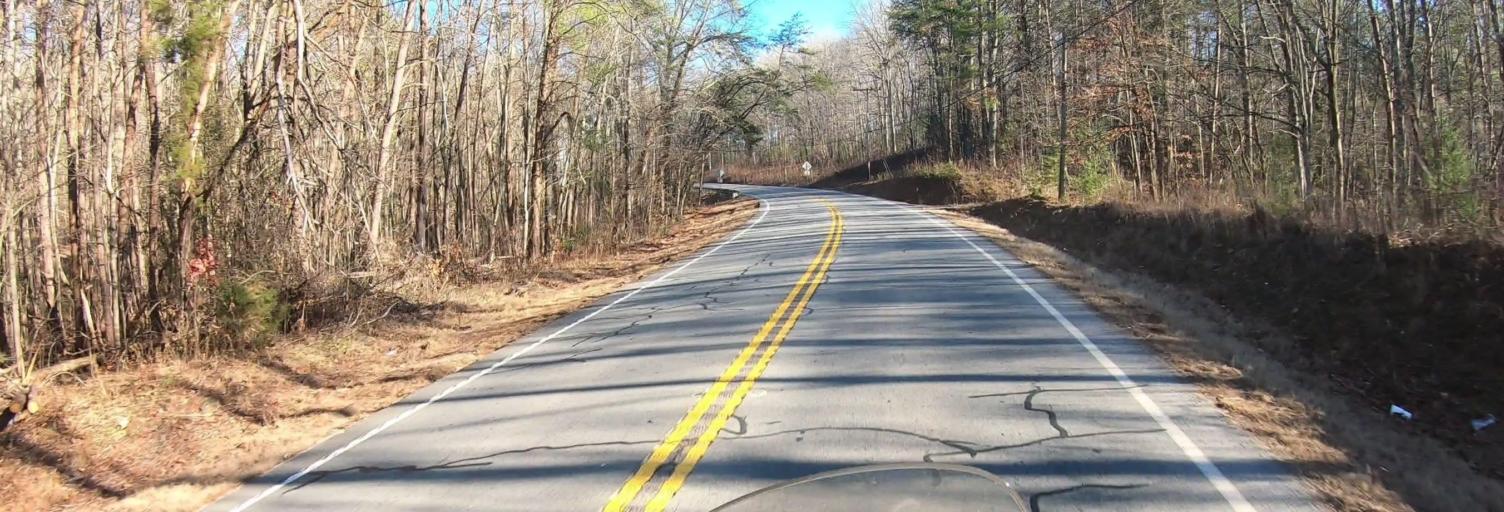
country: US
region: Georgia
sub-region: Fannin County
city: Blue Ridge
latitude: 34.9356
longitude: -84.3110
